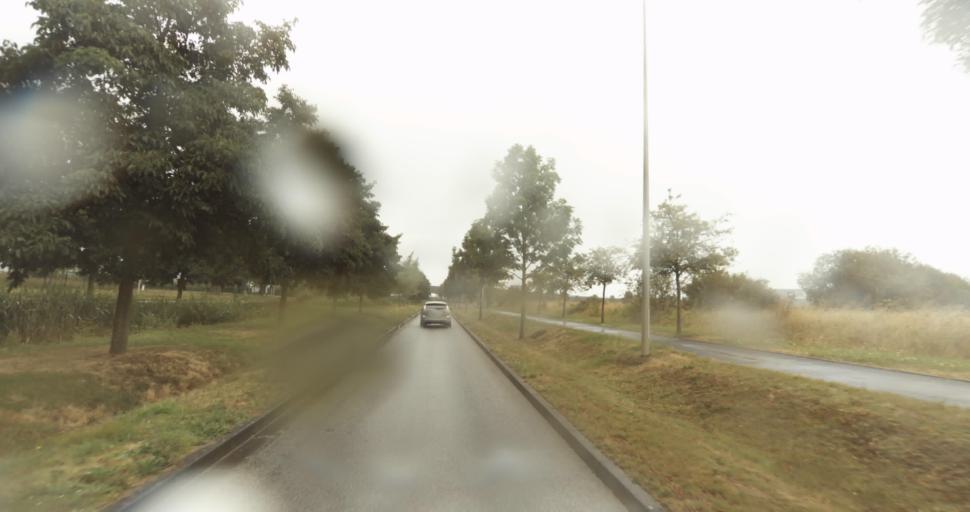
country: FR
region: Haute-Normandie
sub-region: Departement de l'Eure
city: Evreux
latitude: 49.0093
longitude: 1.1813
